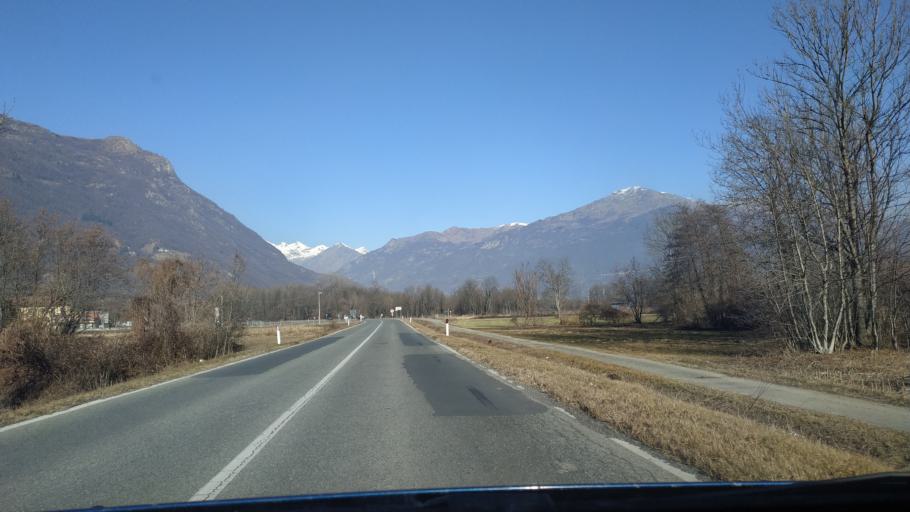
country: IT
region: Piedmont
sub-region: Provincia di Torino
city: Fiorano Canavese
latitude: 45.4819
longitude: 7.8307
